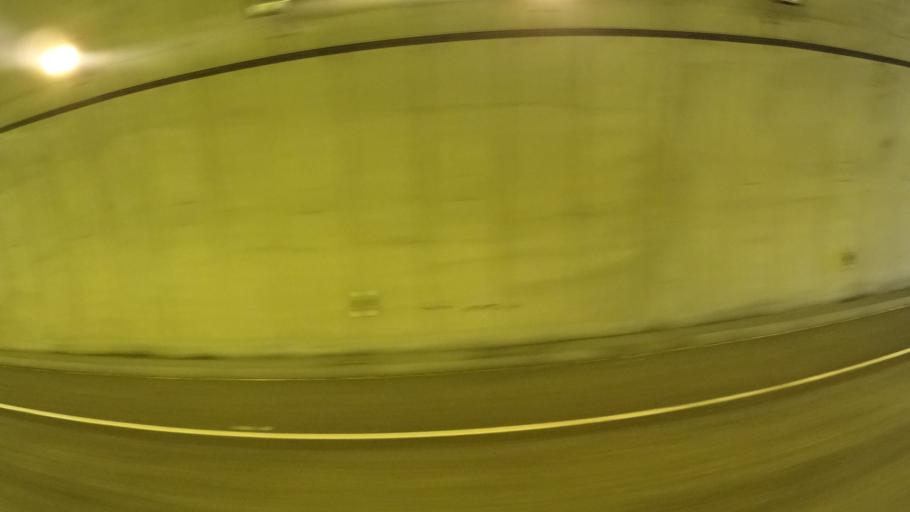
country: ES
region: Castille and Leon
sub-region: Provincia de Leon
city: Balboa
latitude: 42.7351
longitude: -7.0465
